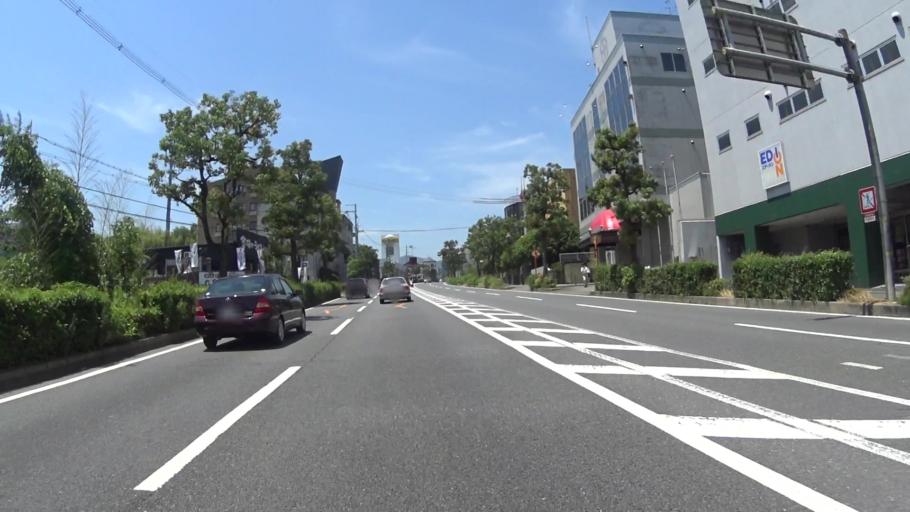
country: JP
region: Kyoto
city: Muko
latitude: 34.9707
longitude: 135.6801
